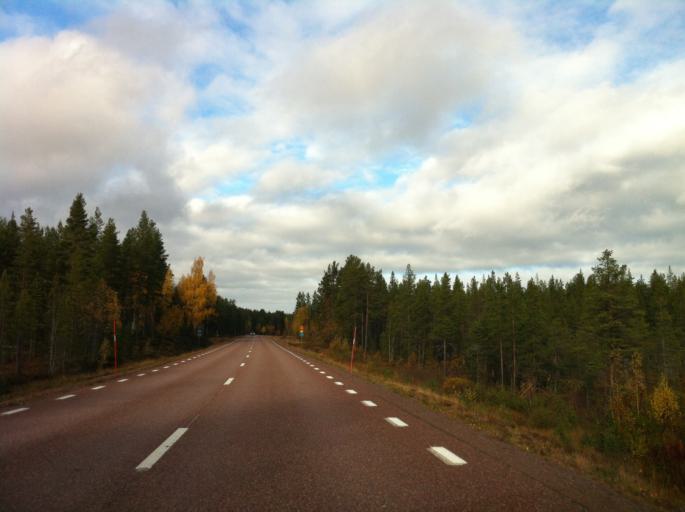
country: SE
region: Dalarna
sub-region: Alvdalens Kommun
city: AElvdalen
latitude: 61.5242
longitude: 13.3632
